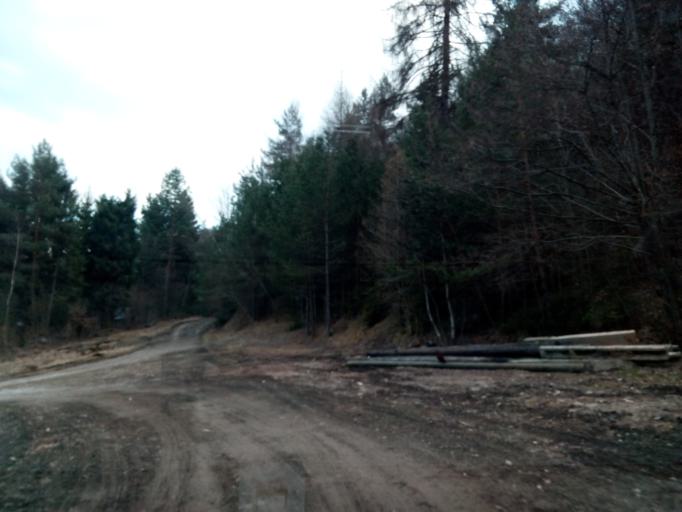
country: SK
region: Kosicky
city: Krompachy
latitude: 48.9531
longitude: 20.8933
